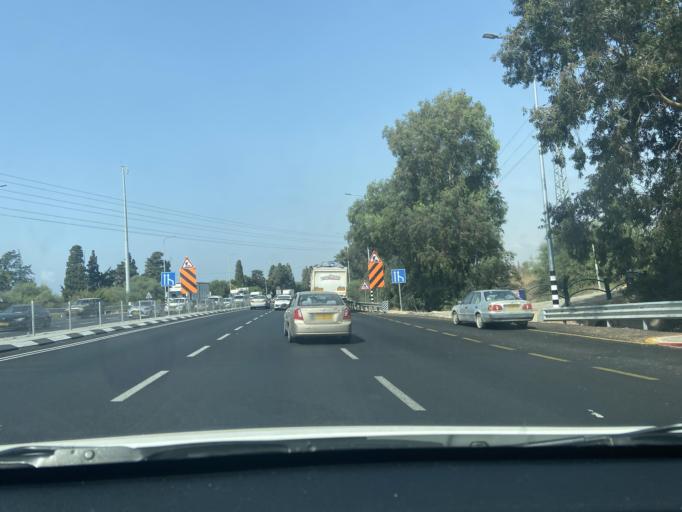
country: IL
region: Northern District
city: `Akko
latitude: 32.9524
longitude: 35.0908
